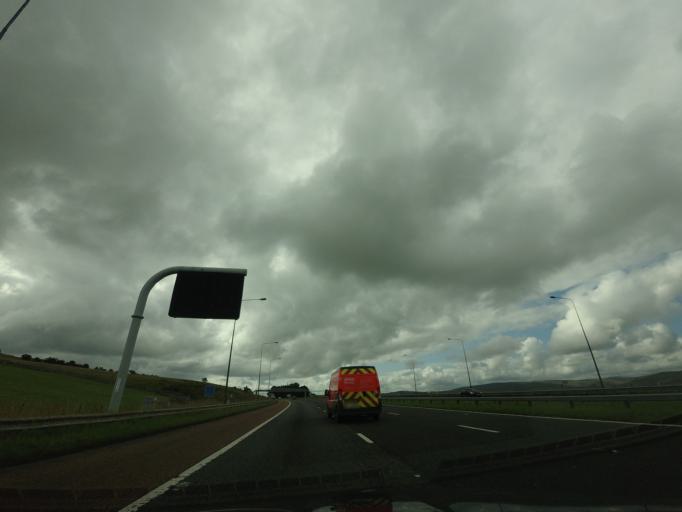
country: GB
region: England
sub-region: Cumbria
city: Penrith
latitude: 54.5239
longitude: -2.6588
